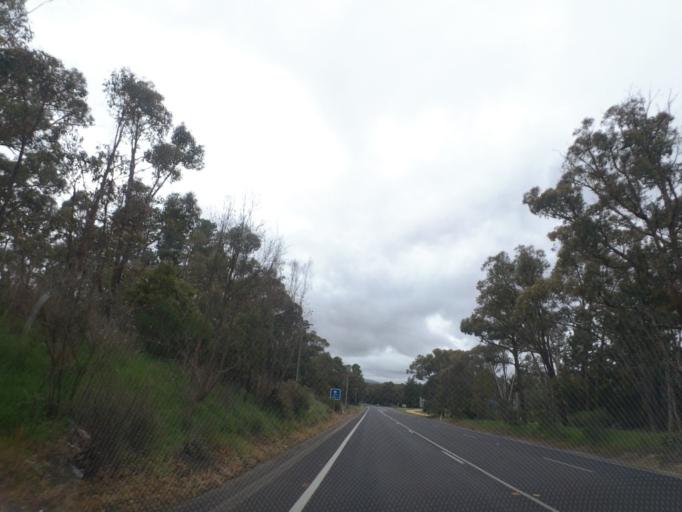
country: AU
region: Victoria
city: Brown Hill
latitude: -37.4455
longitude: 143.8869
